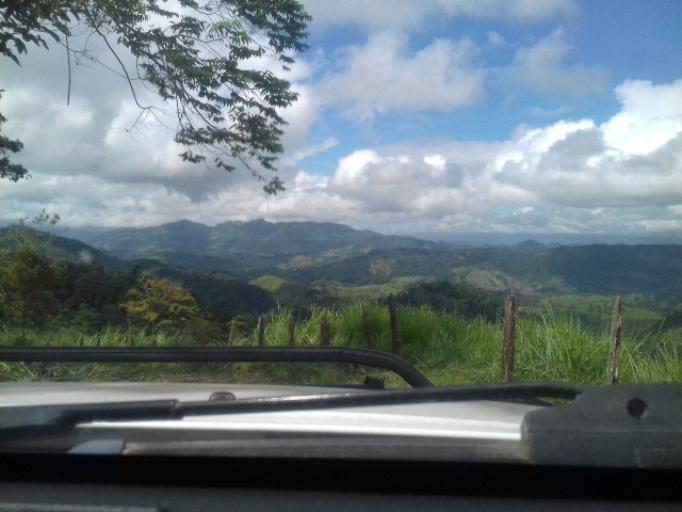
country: NI
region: Atlantico Norte (RAAN)
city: Waslala
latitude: 13.2168
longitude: -85.5755
